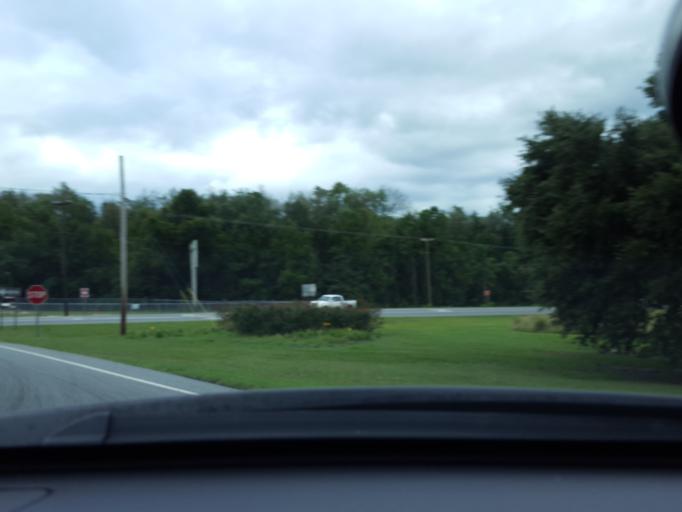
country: US
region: North Carolina
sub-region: Bladen County
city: Elizabethtown
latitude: 34.6494
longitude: -78.5235
